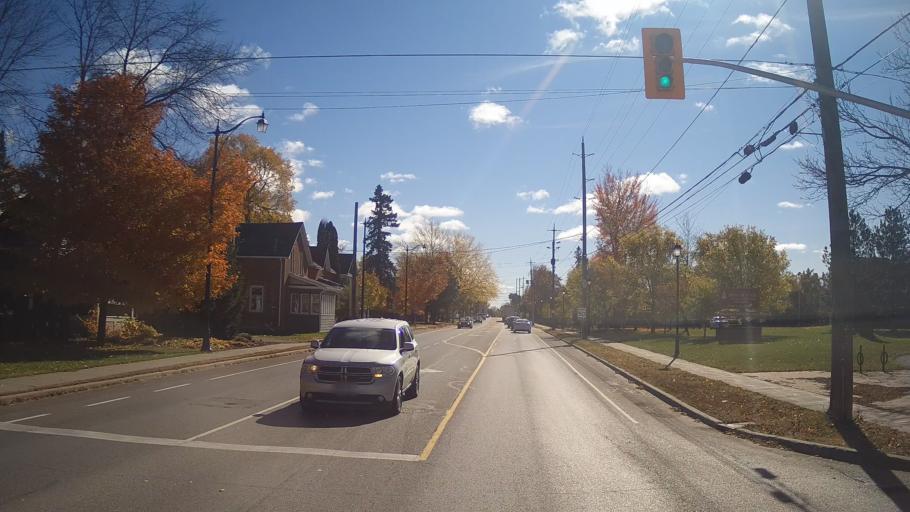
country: CA
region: Ontario
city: Perth
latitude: 44.9055
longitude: -76.2589
